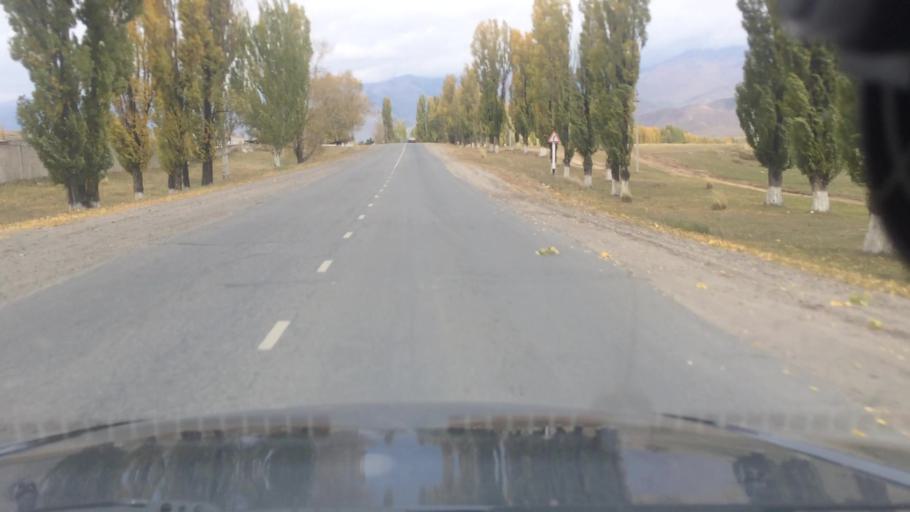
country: KG
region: Ysyk-Koel
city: Tyup
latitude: 42.7409
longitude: 78.3425
